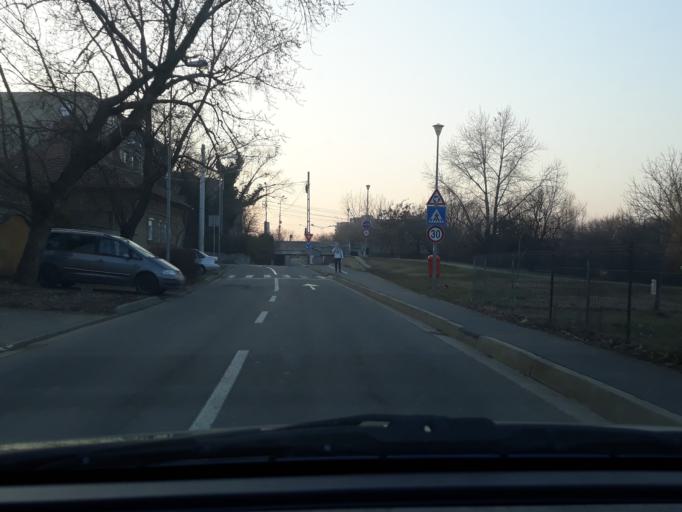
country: RO
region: Bihor
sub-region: Comuna Biharea
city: Oradea
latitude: 47.0636
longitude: 21.9234
